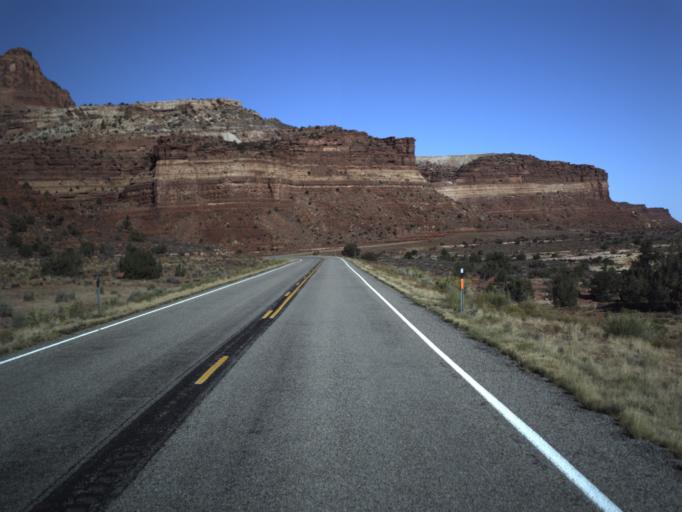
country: US
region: Utah
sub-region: San Juan County
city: Blanding
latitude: 37.7394
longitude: -110.2750
